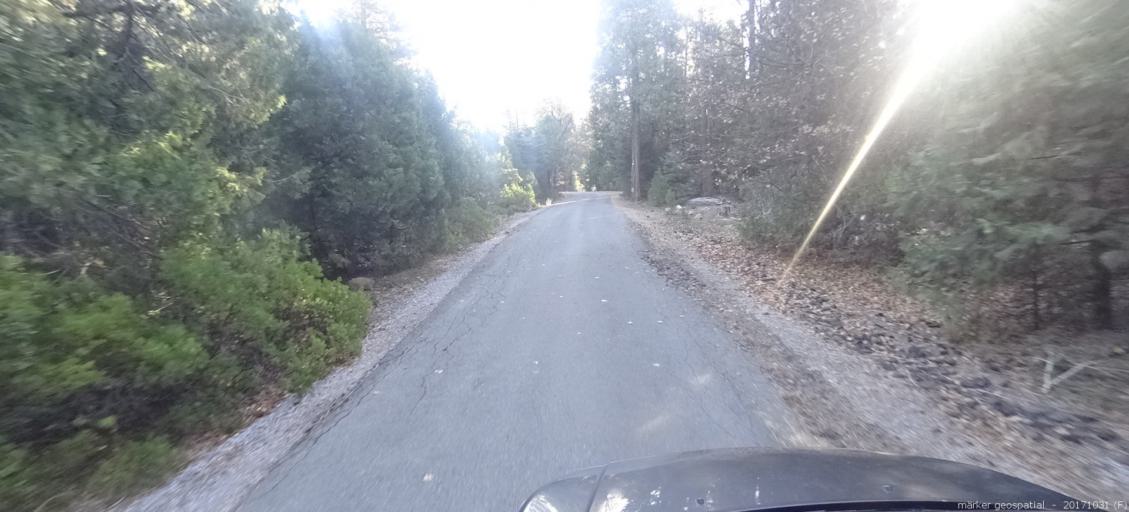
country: US
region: California
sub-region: Shasta County
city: Shingletown
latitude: 40.5238
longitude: -121.7909
